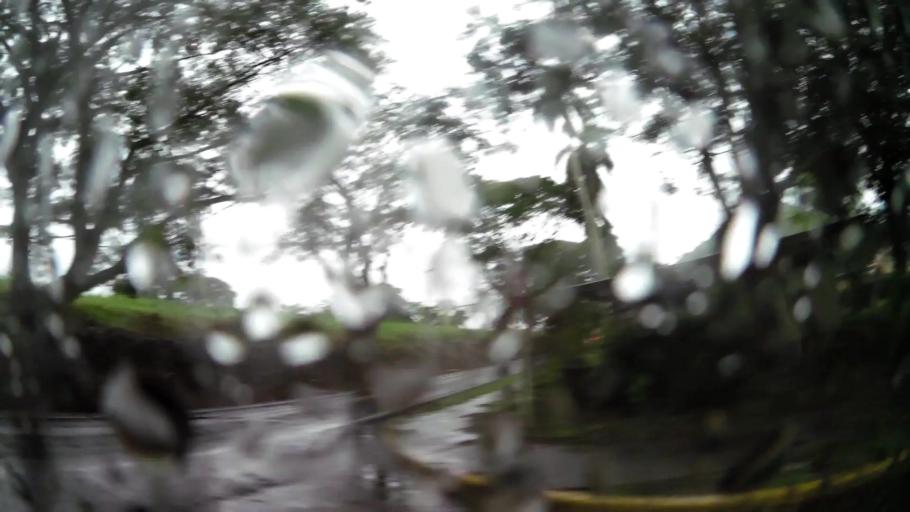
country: PA
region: Panama
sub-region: Distrito de Panama
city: Paraiso
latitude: 9.0184
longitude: -79.6096
